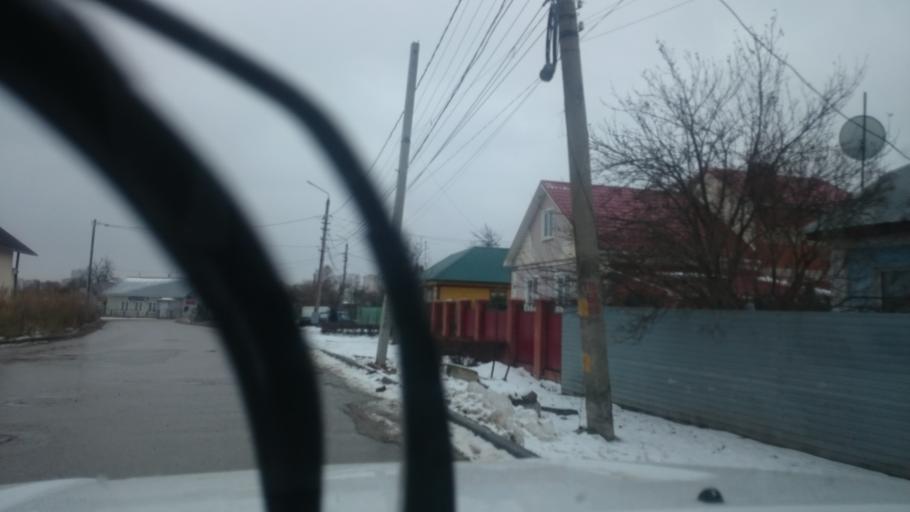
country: RU
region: Tula
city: Tula
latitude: 54.2058
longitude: 37.5672
